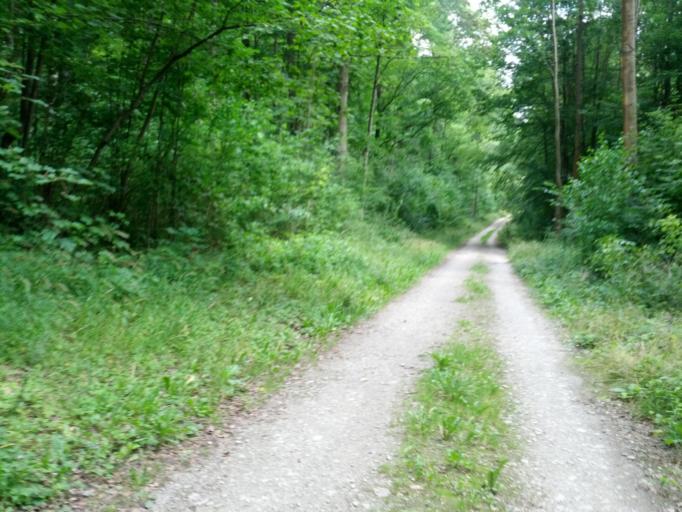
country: DE
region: Thuringia
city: Eisenach
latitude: 50.9884
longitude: 10.3426
